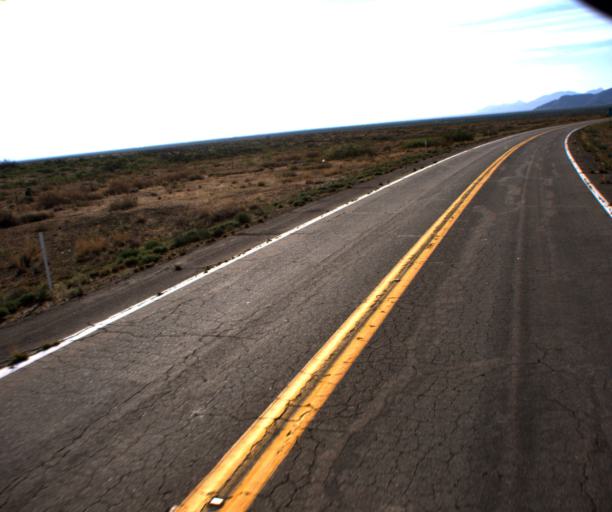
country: US
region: Arizona
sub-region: Cochise County
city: Willcox
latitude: 32.3704
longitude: -109.6263
